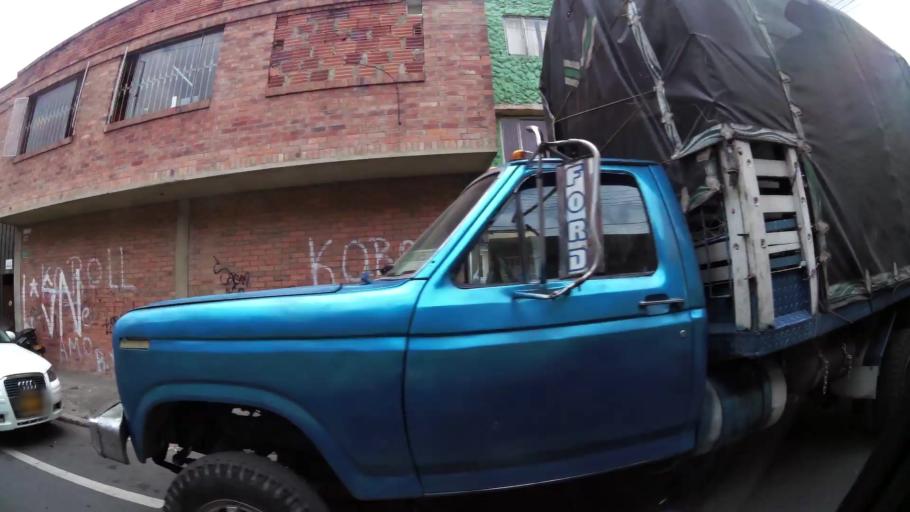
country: CO
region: Cundinamarca
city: Cota
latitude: 4.7489
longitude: -74.0486
